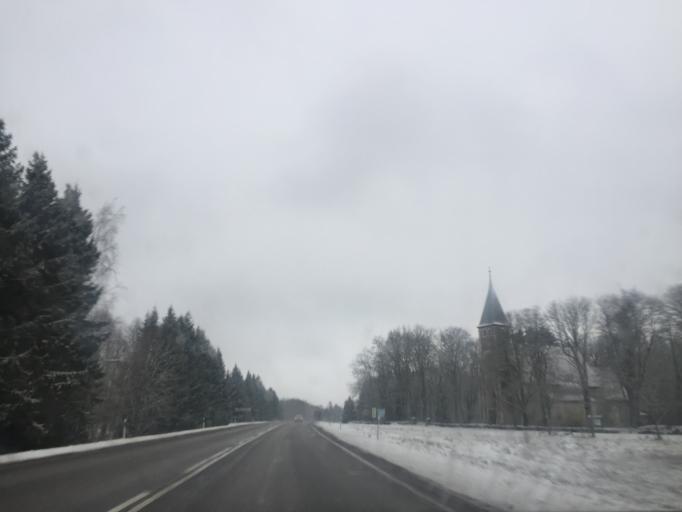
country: EE
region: Laeaene
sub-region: Lihula vald
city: Lihula
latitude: 58.6358
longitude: 23.6889
